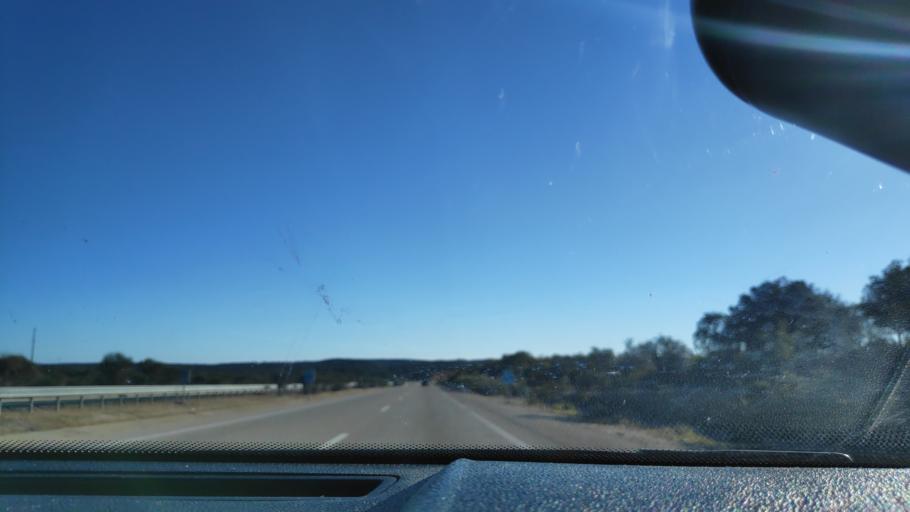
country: ES
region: Andalusia
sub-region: Provincia de Huelva
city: Santa Olalla del Cala
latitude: 37.8673
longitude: -6.2193
